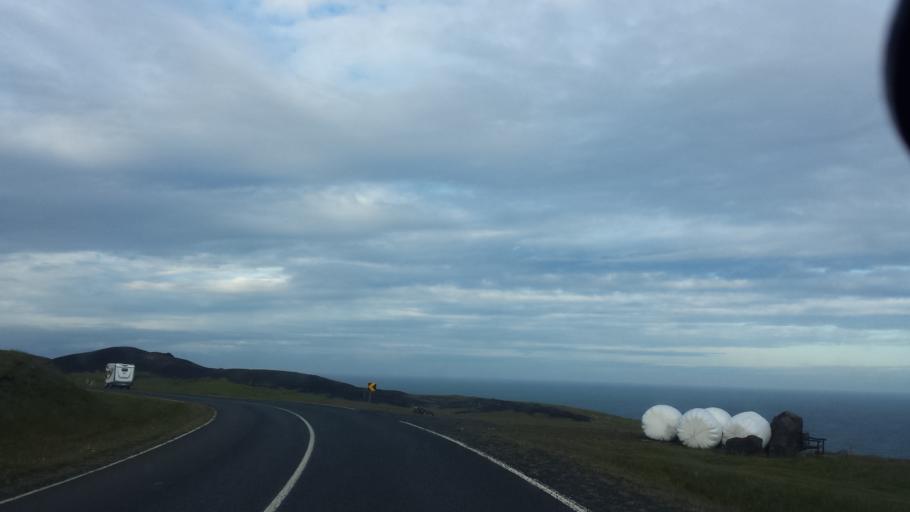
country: IS
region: South
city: Vestmannaeyjar
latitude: 63.4248
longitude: -20.2645
